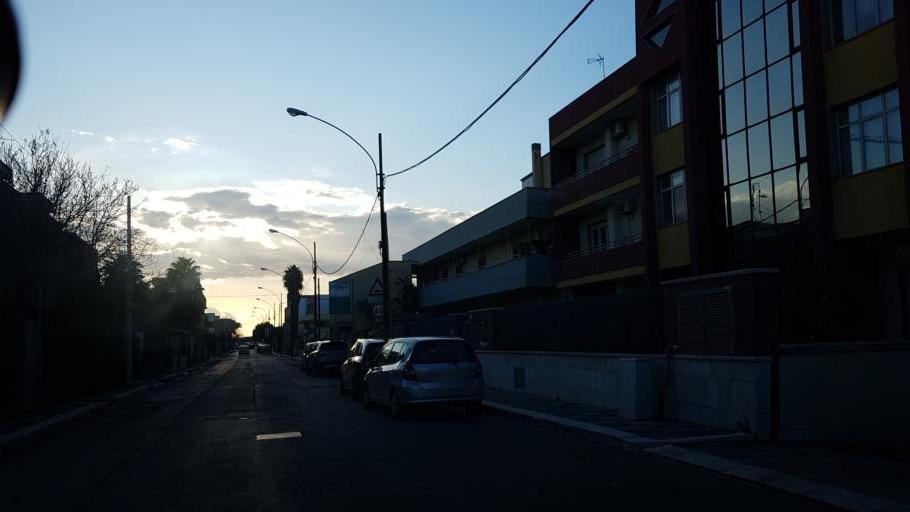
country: IT
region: Apulia
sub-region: Provincia di Lecce
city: Surbo
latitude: 40.3924
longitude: 18.1286
